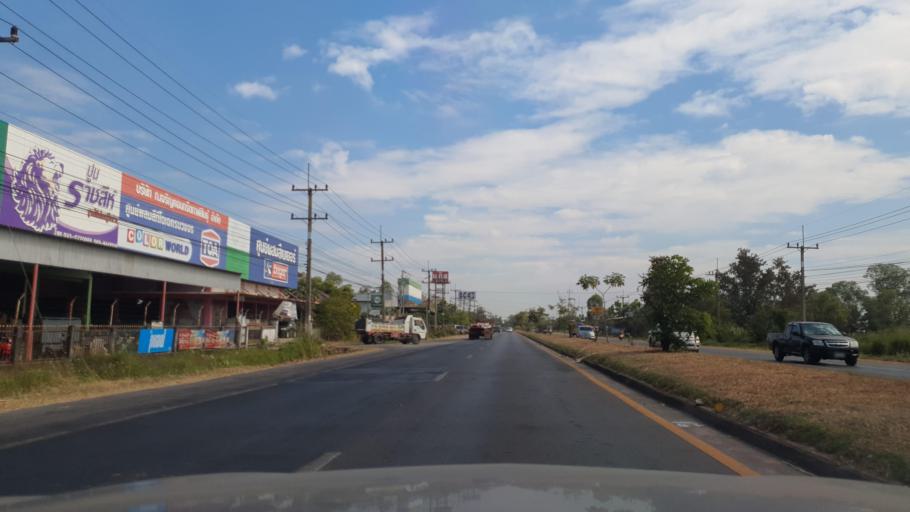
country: TH
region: Kalasin
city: Kalasin
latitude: 16.4073
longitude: 103.4476
